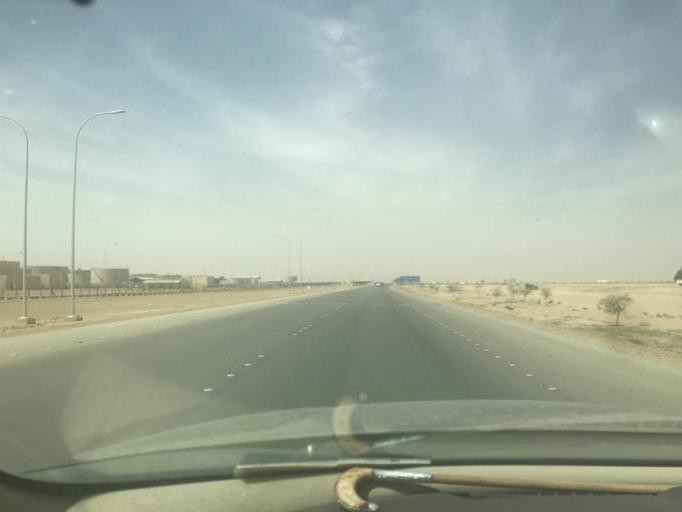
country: SA
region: Ar Riyad
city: Riyadh
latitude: 24.9795
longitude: 46.6851
